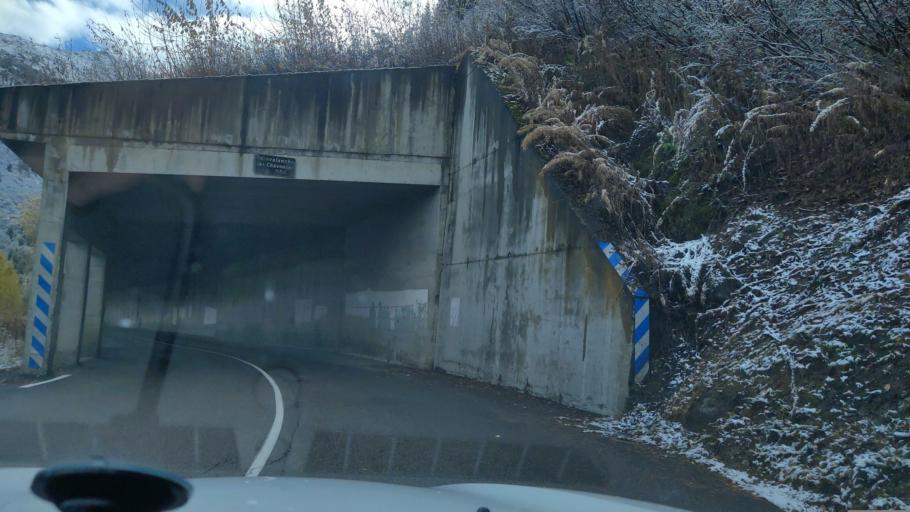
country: FR
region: Rhone-Alpes
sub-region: Departement de la Savoie
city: Seez
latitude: 45.5894
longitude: 6.8280
